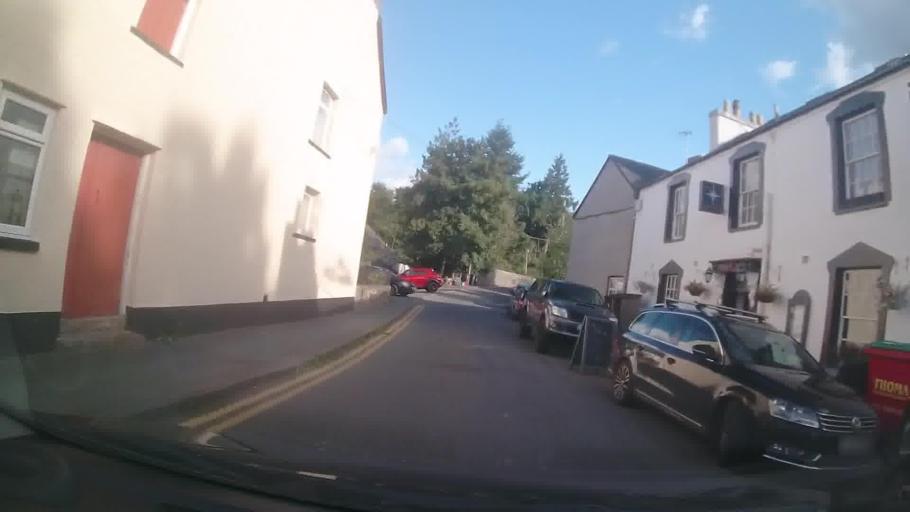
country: GB
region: Wales
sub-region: Sir Powys
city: Brecon
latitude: 51.8951
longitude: -3.2888
